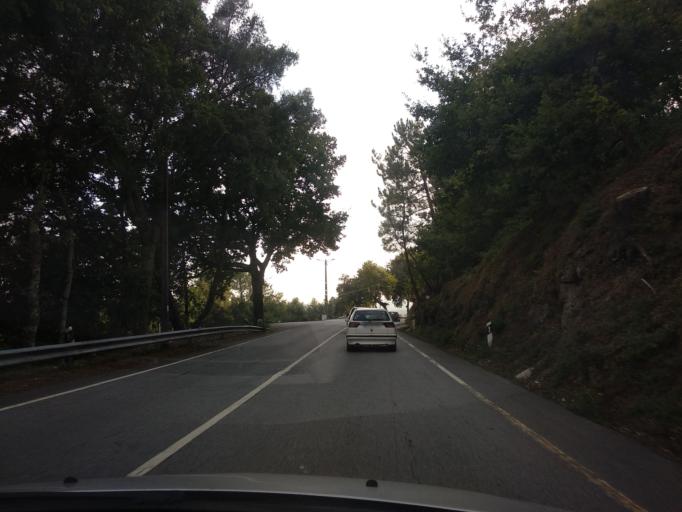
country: PT
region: Braga
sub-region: Povoa de Lanhoso
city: Povoa de Lanhoso
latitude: 41.6106
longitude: -8.2594
